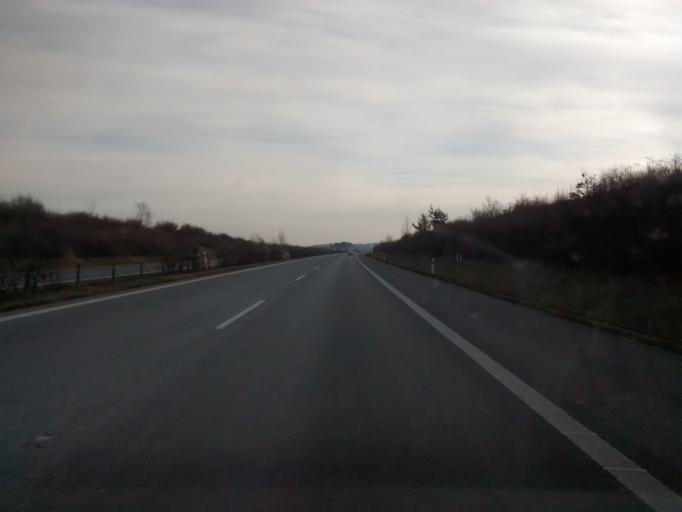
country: CZ
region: Ustecky
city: Roudnice nad Labem
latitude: 50.4110
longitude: 14.2164
